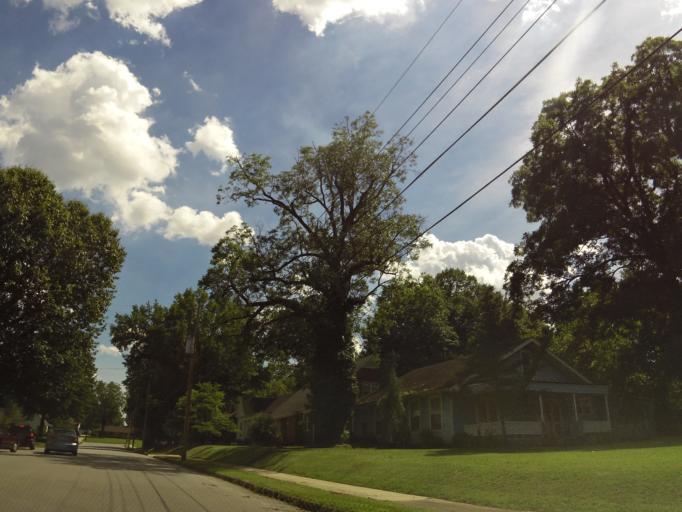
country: US
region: Tennessee
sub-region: Gibson County
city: Trenton
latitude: 35.9739
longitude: -88.9431
